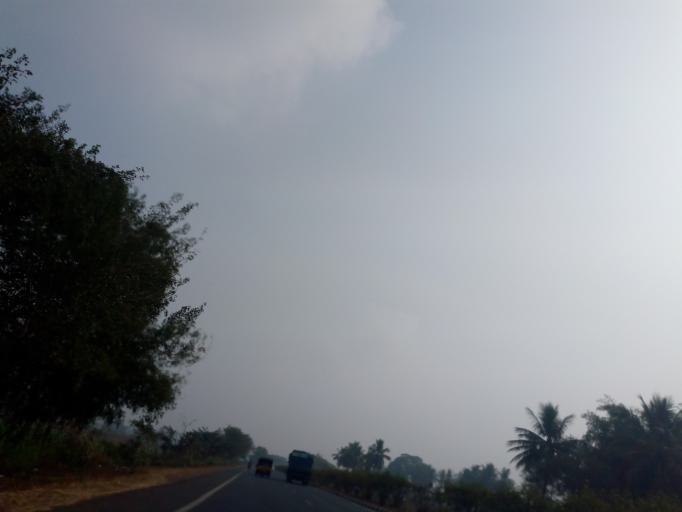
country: IN
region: Andhra Pradesh
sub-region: West Godavari
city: Tadepallegudem
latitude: 16.8163
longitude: 81.3835
